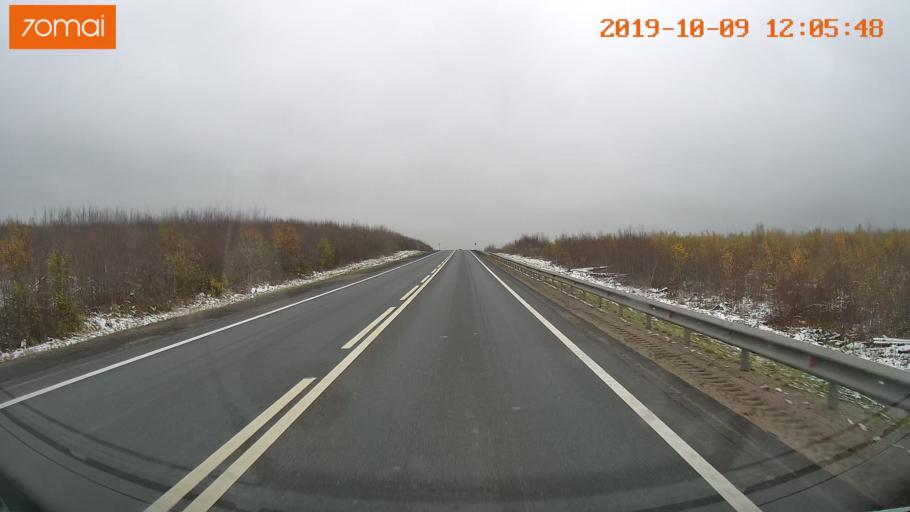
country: RU
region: Jaroslavl
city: Prechistoye
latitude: 58.6241
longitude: 40.3309
